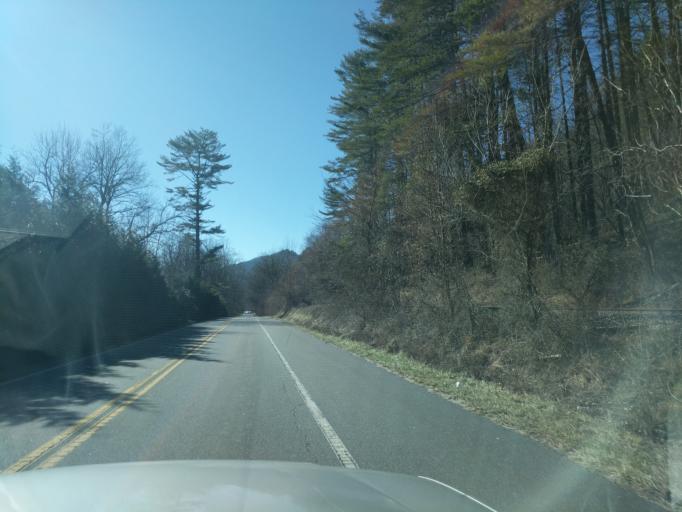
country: US
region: North Carolina
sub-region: Graham County
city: Robbinsville
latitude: 35.2869
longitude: -83.6677
